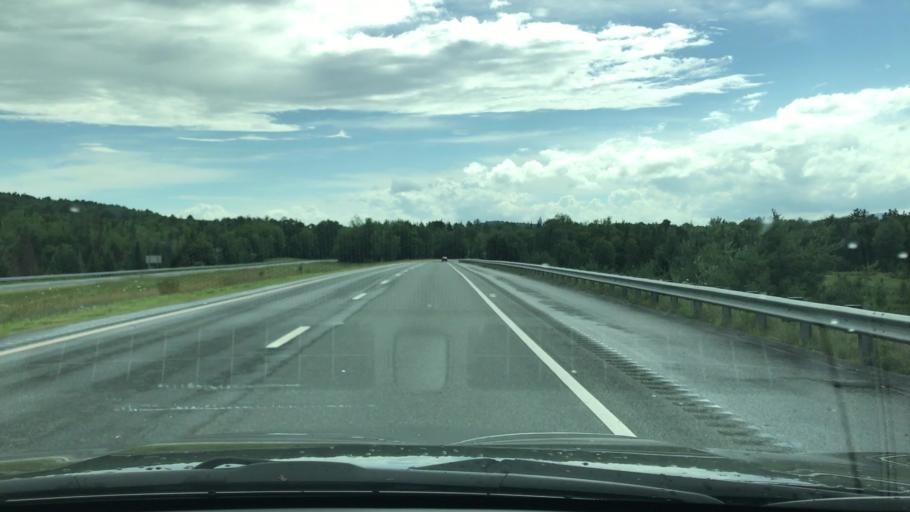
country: US
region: New Hampshire
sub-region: Grafton County
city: Littleton
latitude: 44.3172
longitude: -71.8318
